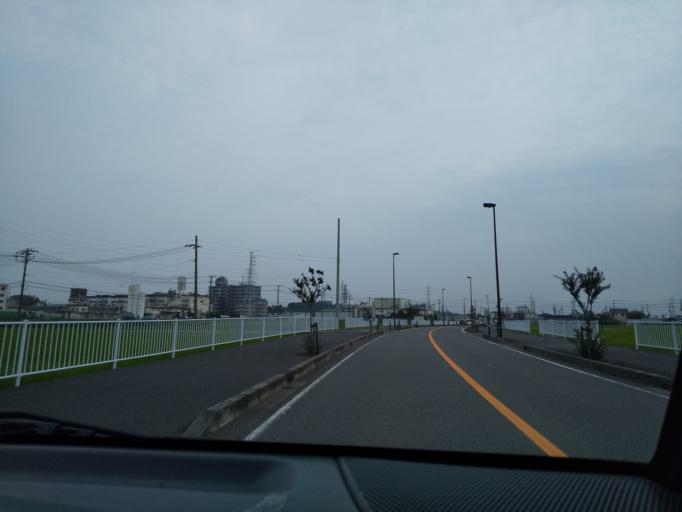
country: JP
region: Kanagawa
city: Atsugi
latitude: 35.4249
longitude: 139.3914
